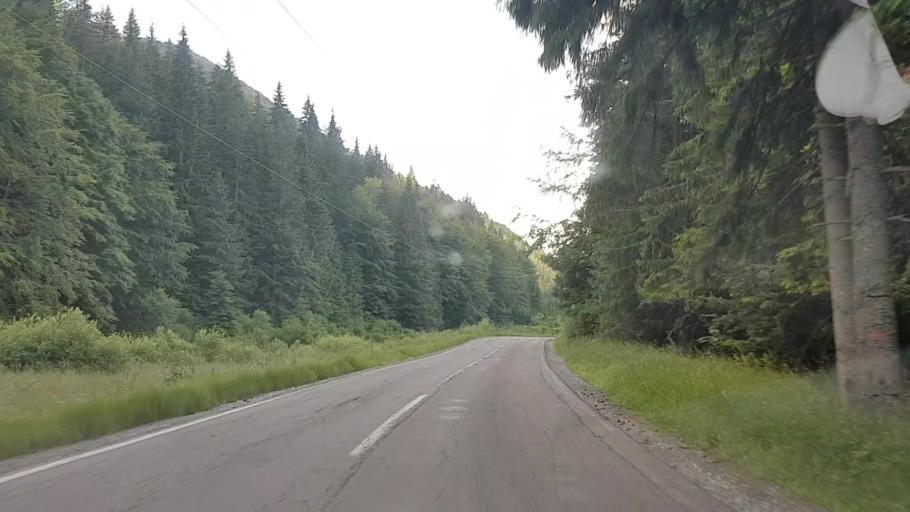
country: RO
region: Harghita
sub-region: Comuna Varsag
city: Varsag
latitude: 46.6315
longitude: 25.2641
